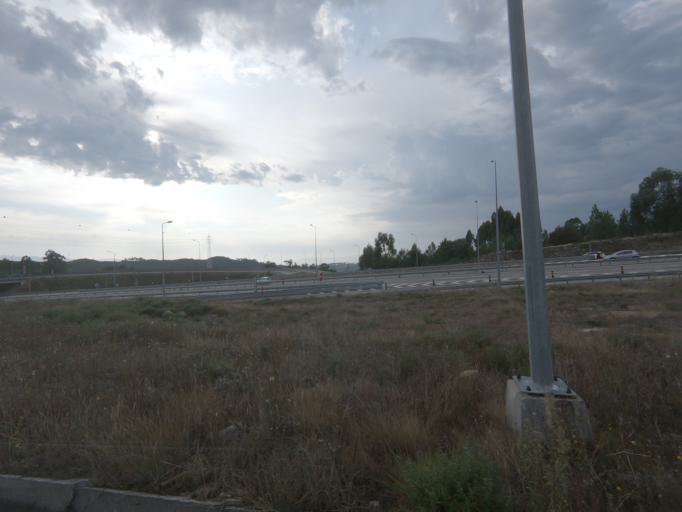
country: PT
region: Viseu
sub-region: Viseu
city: Campo
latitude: 40.7082
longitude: -7.9433
